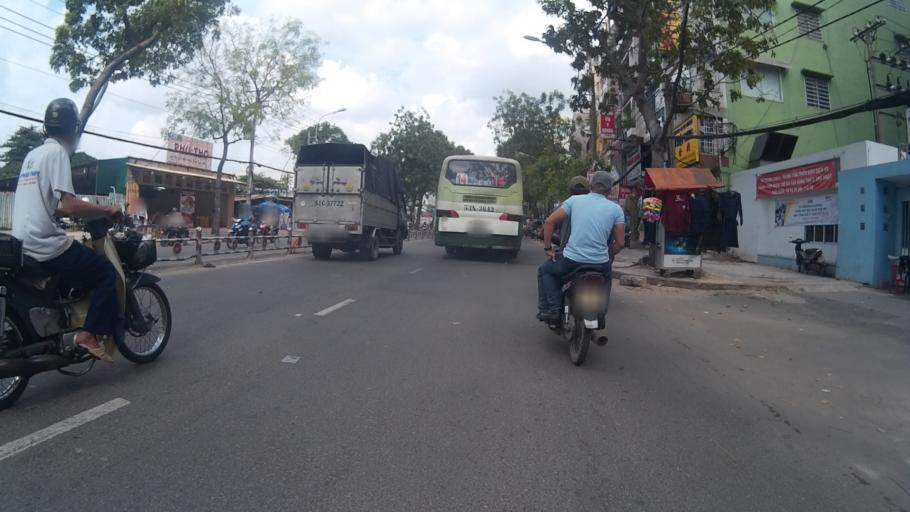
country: VN
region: Ho Chi Minh City
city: Quan Muoi
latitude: 10.7626
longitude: 106.6578
